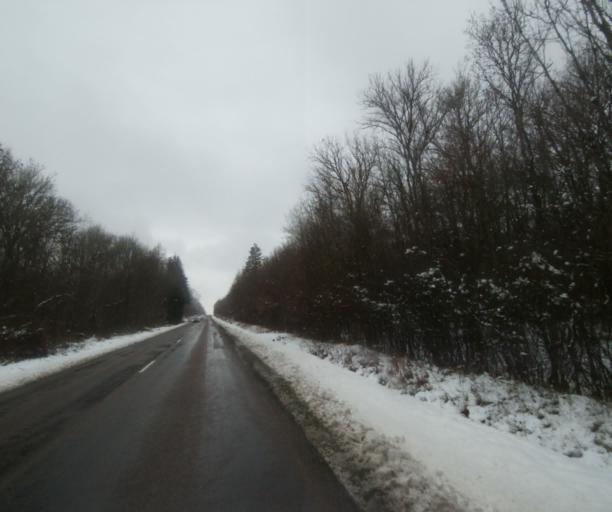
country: FR
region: Champagne-Ardenne
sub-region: Departement de la Haute-Marne
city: Wassy
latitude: 48.4958
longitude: 4.9267
